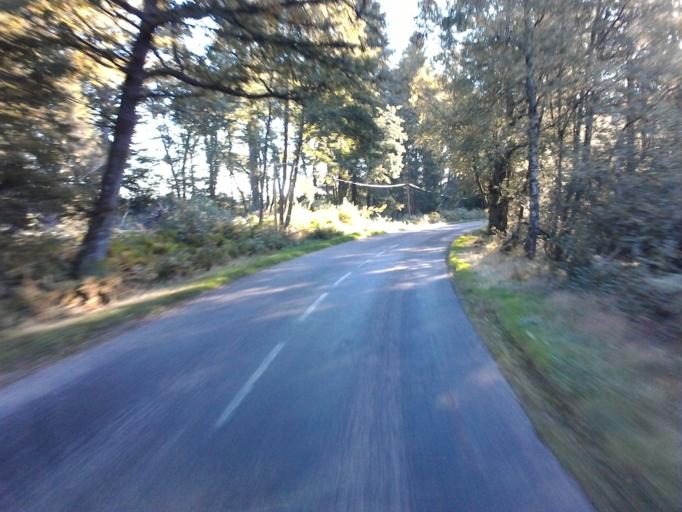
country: FR
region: Bourgogne
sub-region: Departement de la Cote-d'Or
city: Saulieu
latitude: 47.2709
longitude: 4.1150
